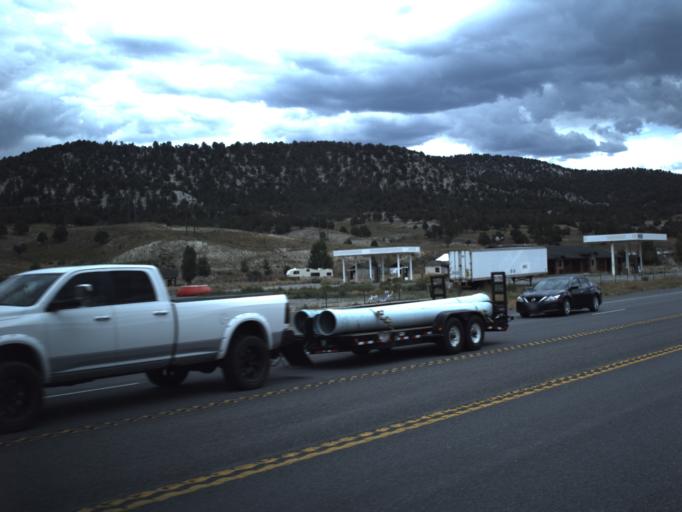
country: US
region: Utah
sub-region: Utah County
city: Mapleton
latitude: 39.9744
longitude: -111.3400
